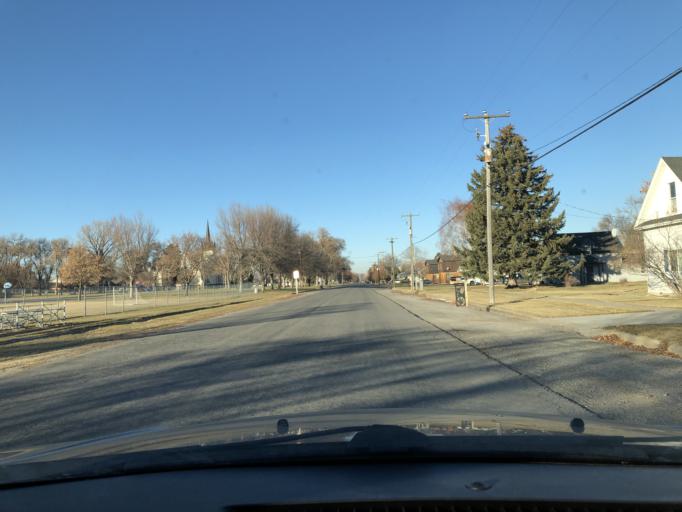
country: US
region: Utah
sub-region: Cache County
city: Wellsville
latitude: 41.6347
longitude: -111.9317
